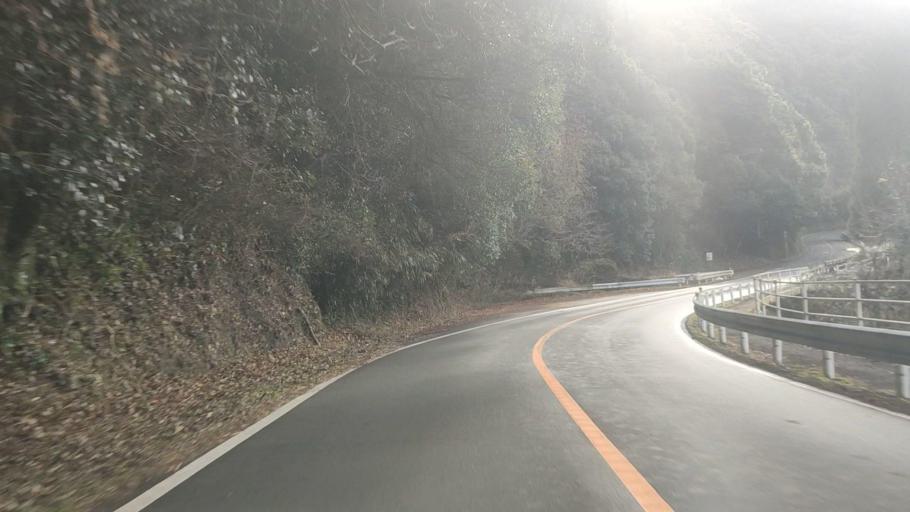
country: JP
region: Kumamoto
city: Hitoyoshi
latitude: 32.3016
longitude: 130.8459
